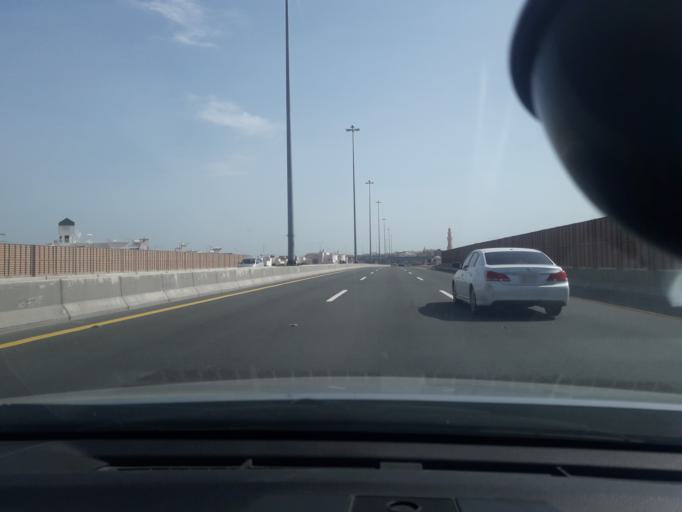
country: SA
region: Al Madinah al Munawwarah
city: Medina
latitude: 24.4445
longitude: 39.6432
